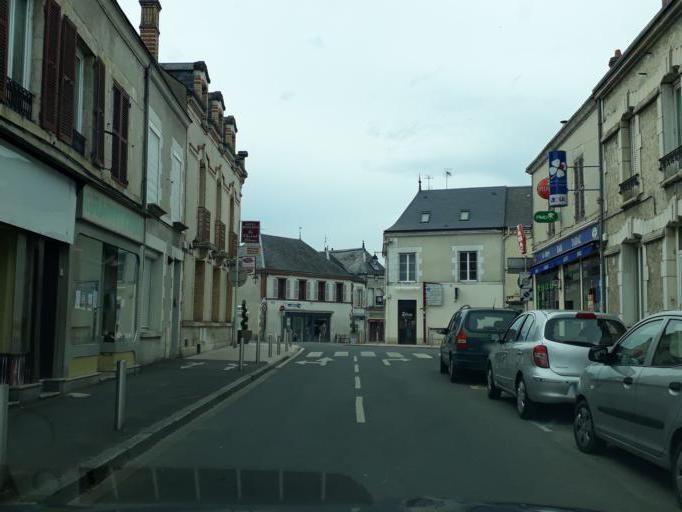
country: FR
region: Centre
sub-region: Departement du Loiret
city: Jargeau
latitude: 47.8647
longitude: 2.1218
